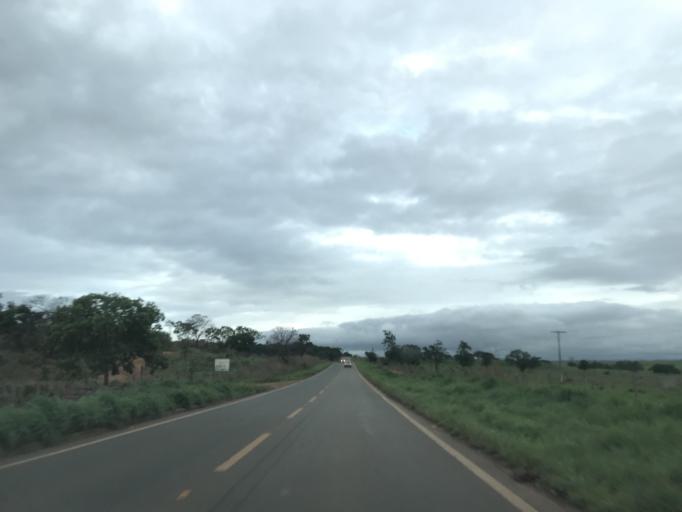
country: BR
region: Goias
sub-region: Luziania
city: Luziania
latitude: -16.2801
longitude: -47.9966
